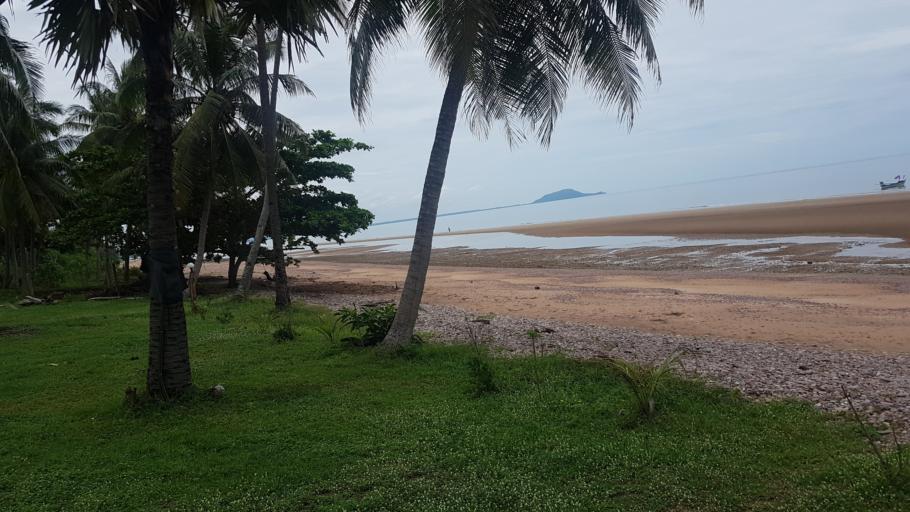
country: TH
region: Prachuap Khiri Khan
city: Bang Saphan Noi
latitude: 11.0577
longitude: 99.4961
